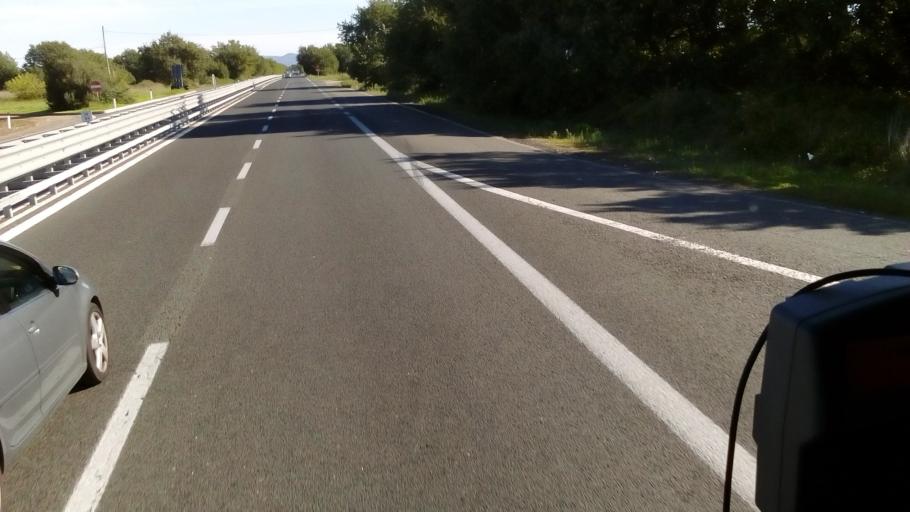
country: IT
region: Latium
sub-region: Provincia di Viterbo
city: Tarquinia
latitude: 42.2924
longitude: 11.6809
